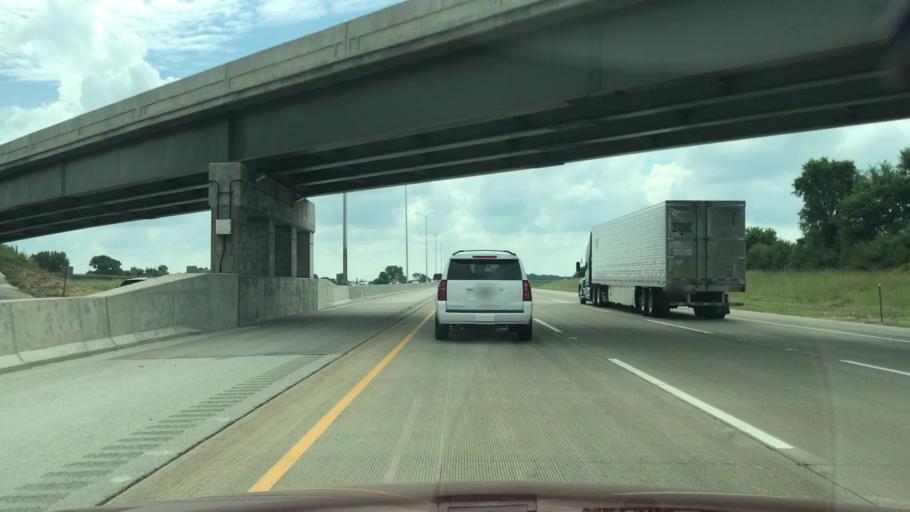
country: US
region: Illinois
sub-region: McHenry County
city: Marengo
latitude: 42.1947
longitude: -88.6671
